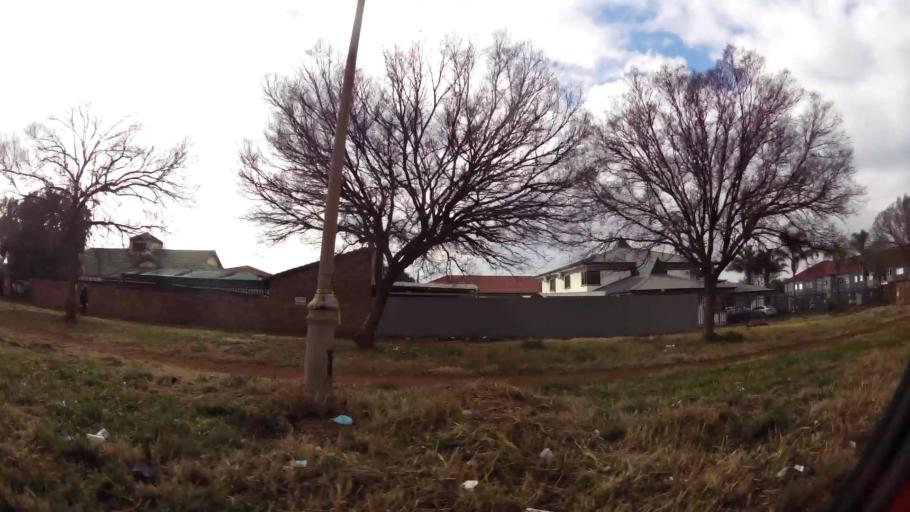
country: ZA
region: Gauteng
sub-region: Sedibeng District Municipality
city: Vanderbijlpark
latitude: -26.7001
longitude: 27.8313
